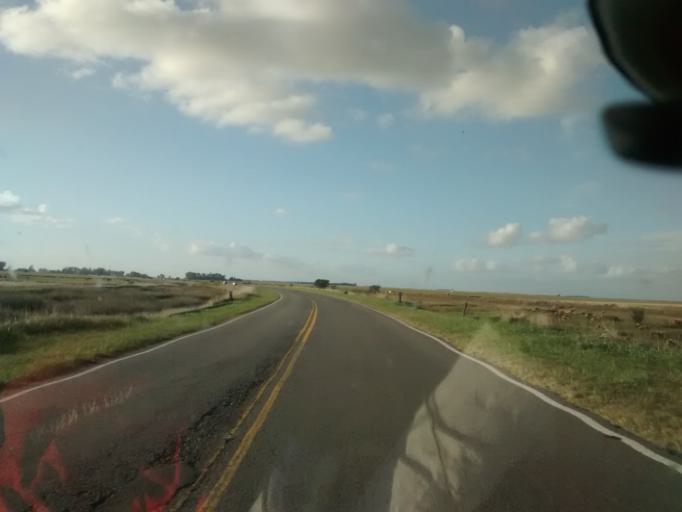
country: AR
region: Buenos Aires
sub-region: Partido de General Belgrano
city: General Belgrano
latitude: -36.1273
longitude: -58.5928
